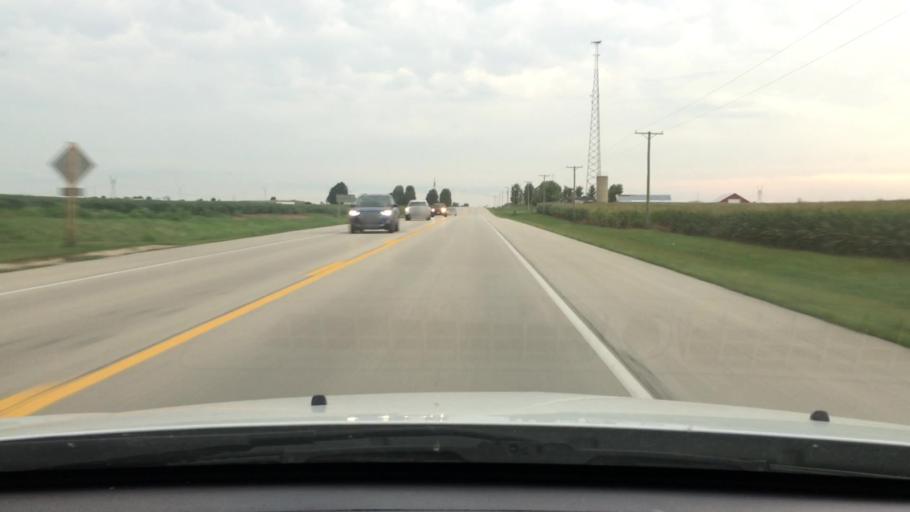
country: US
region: Illinois
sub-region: DeKalb County
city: Waterman
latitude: 41.7922
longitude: -88.7541
